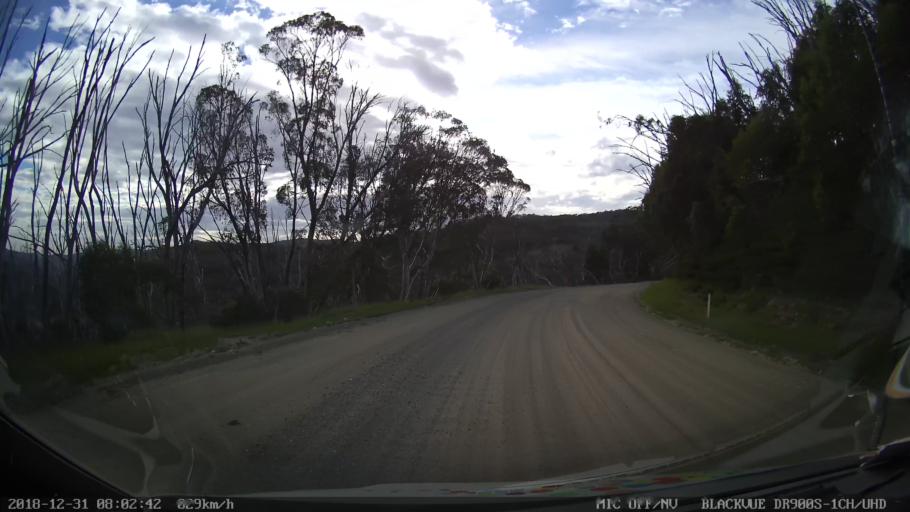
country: AU
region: New South Wales
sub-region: Snowy River
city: Jindabyne
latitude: -36.3608
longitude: 148.4025
